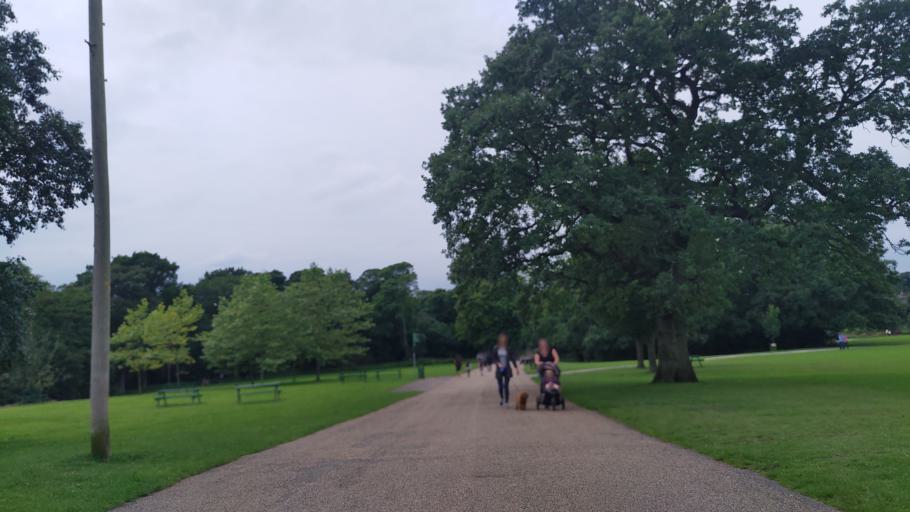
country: GB
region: England
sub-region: Lancashire
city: Chorley
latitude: 53.6577
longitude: -2.6425
